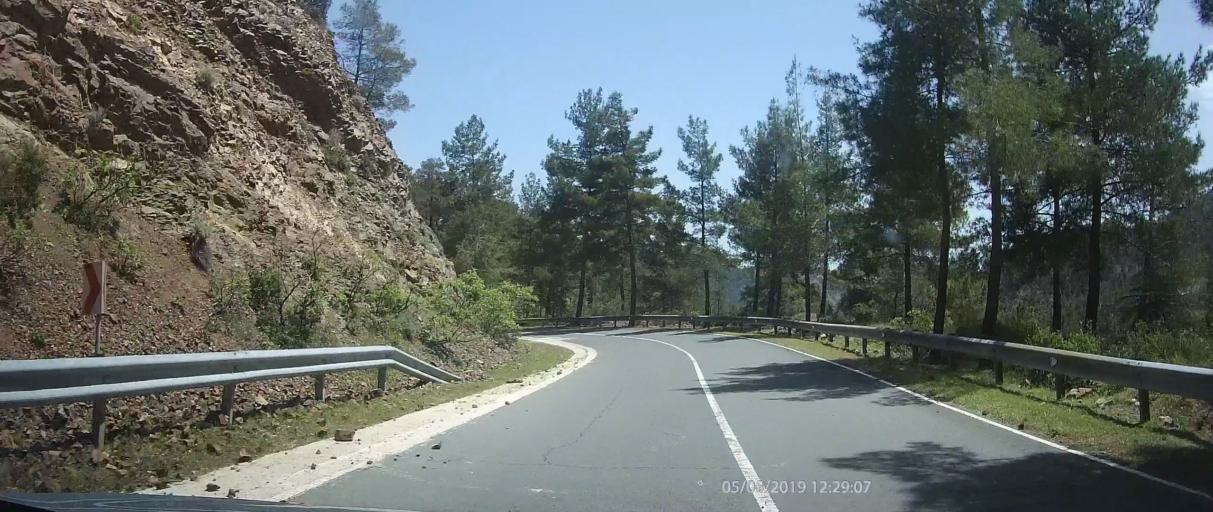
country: CY
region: Lefkosia
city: Kakopetria
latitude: 34.9812
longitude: 32.7444
